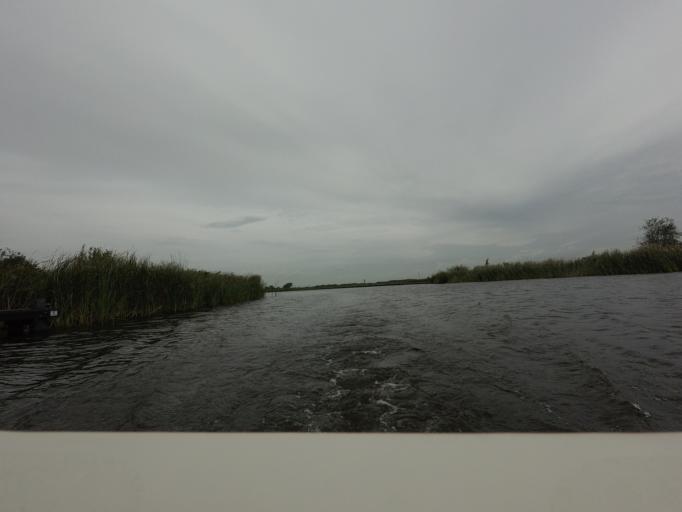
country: NL
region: Friesland
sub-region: Gemeente Boarnsterhim
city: Warten
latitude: 53.1135
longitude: 5.8881
